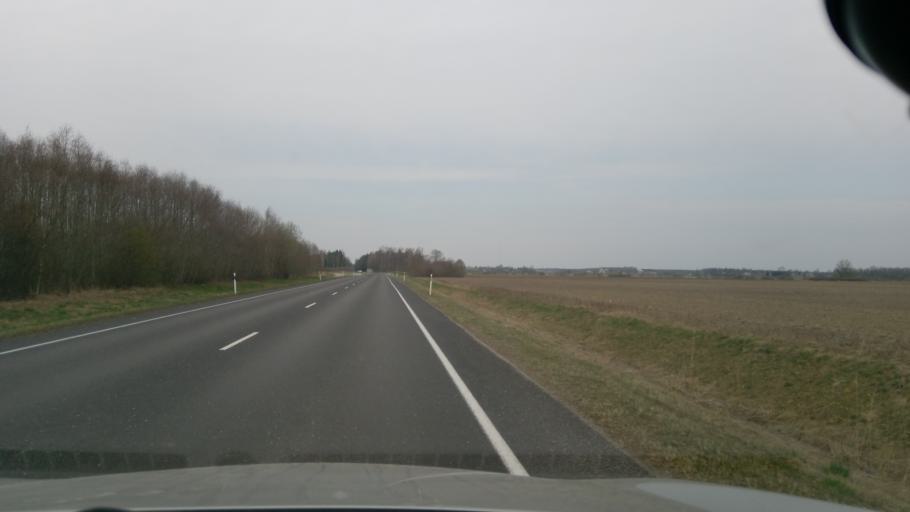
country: EE
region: Viljandimaa
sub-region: Vohma linn
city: Vohma
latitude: 58.7340
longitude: 25.5907
